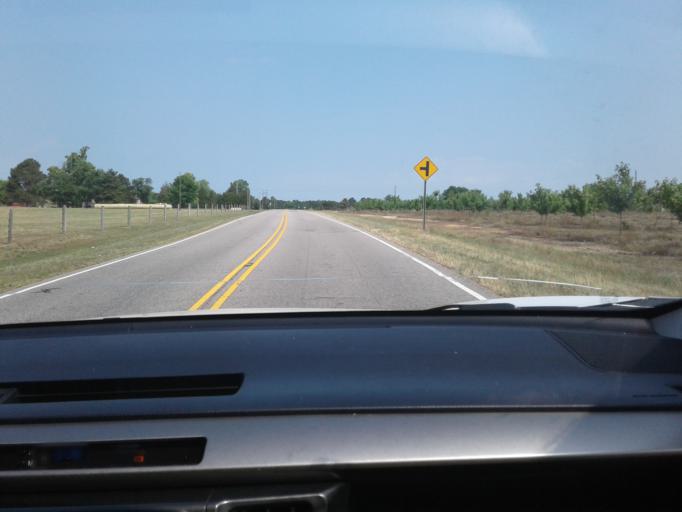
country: US
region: North Carolina
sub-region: Harnett County
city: Coats
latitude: 35.4503
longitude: -78.6863
